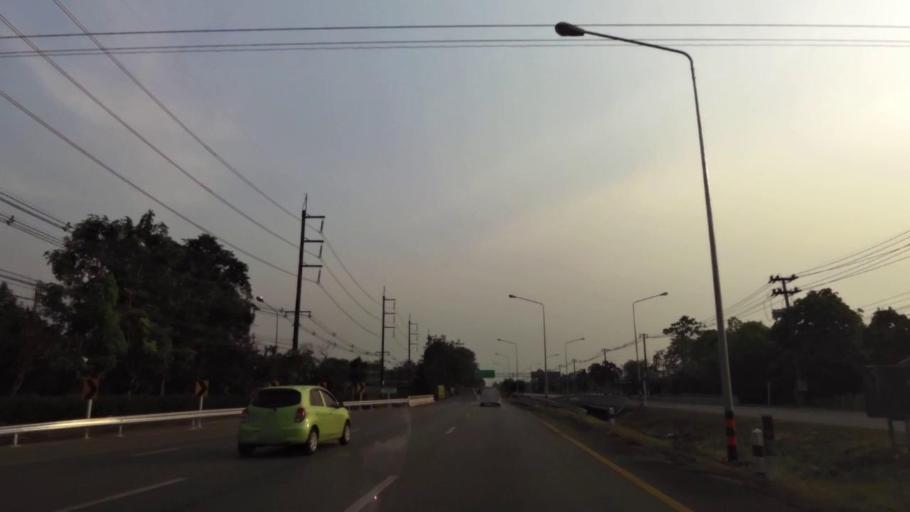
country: TH
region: Chanthaburi
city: Khlung
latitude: 12.5083
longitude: 102.1694
